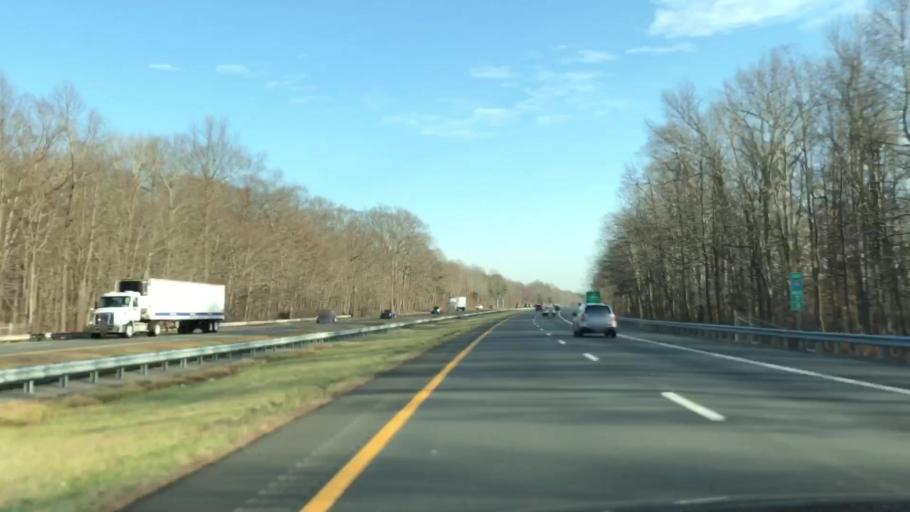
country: US
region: New Jersey
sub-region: Monmouth County
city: Allentown
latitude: 40.1901
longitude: -74.5837
